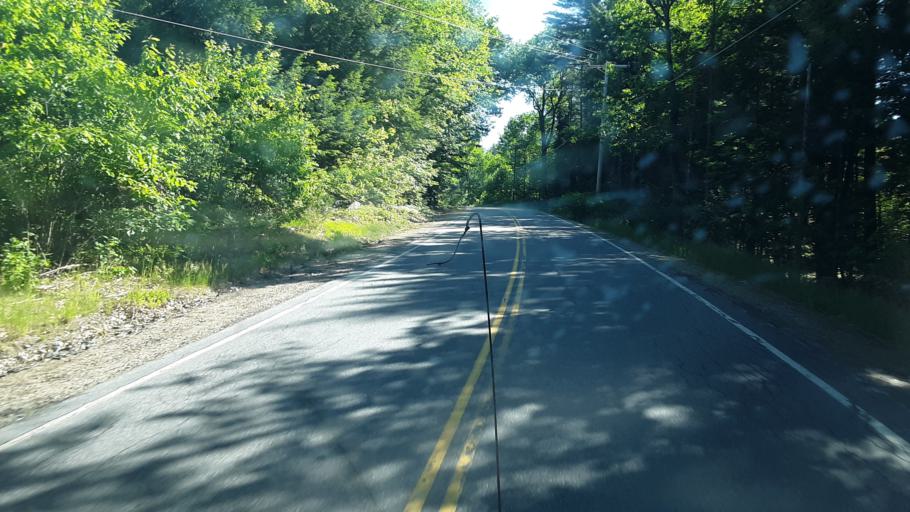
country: US
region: New Hampshire
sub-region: Grafton County
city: North Haverhill
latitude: 44.0871
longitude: -71.9538
